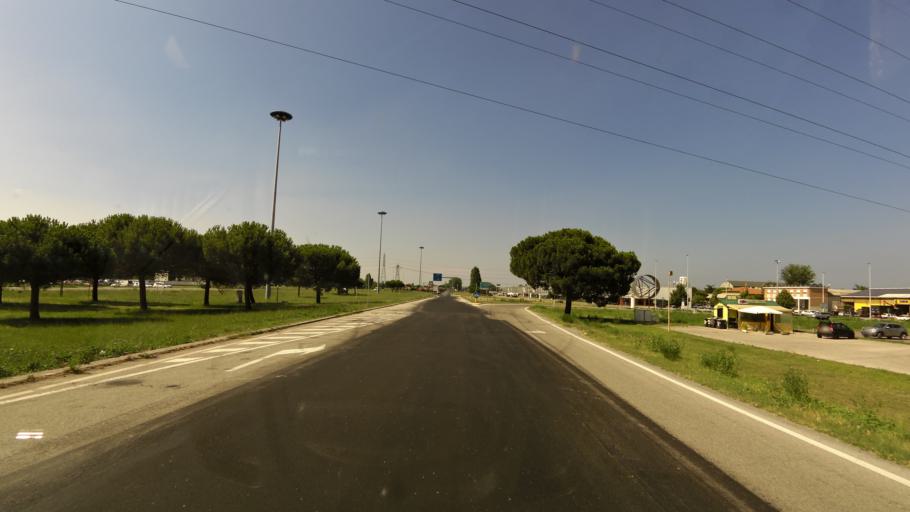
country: IT
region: Emilia-Romagna
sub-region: Provincia di Ravenna
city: Ravenna
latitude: 44.4477
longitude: 12.2102
